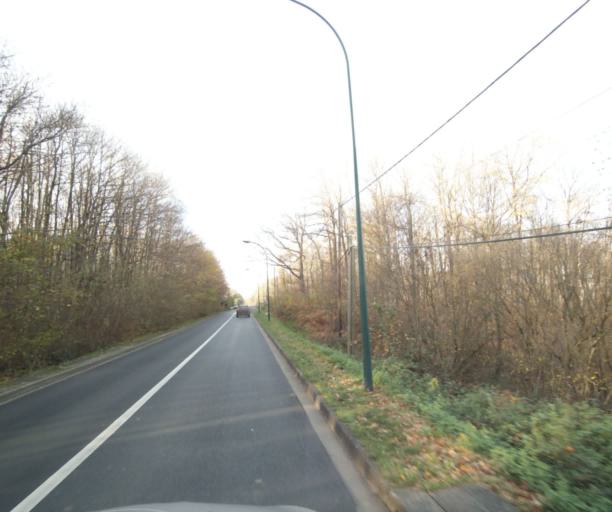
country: FR
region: Ile-de-France
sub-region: Departement du Val-d'Oise
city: Courdimanche
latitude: 49.0104
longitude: 2.0043
